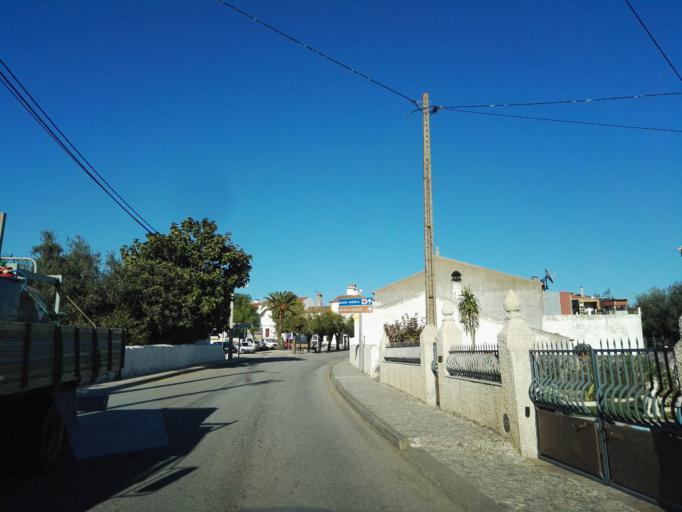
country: PT
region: Evora
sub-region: Estremoz
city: Estremoz
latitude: 38.7646
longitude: -7.7169
